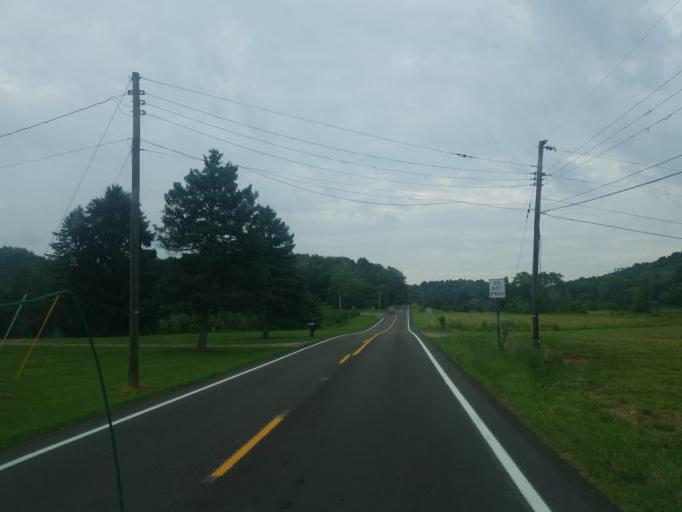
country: US
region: Ohio
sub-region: Carroll County
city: Lake Mohawk
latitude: 40.6658
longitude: -81.2458
